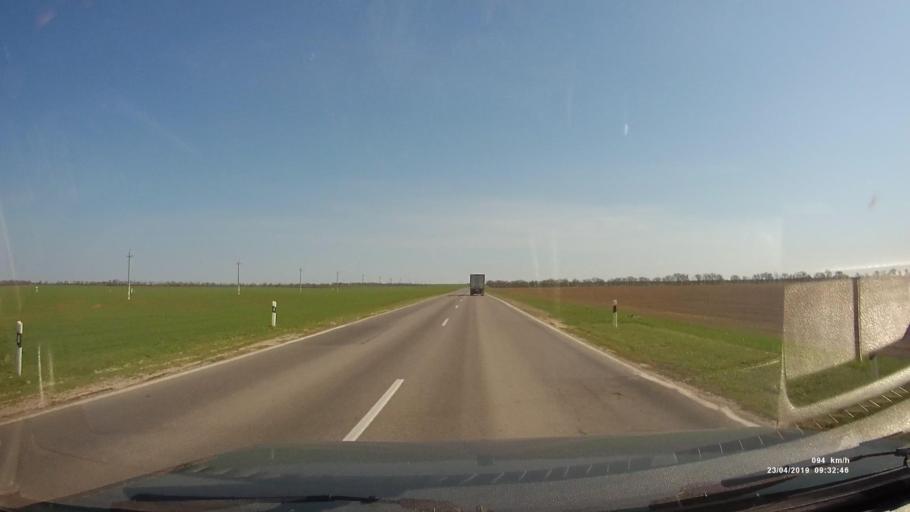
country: RU
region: Rostov
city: Gundorovskiy
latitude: 46.7937
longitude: 41.8398
